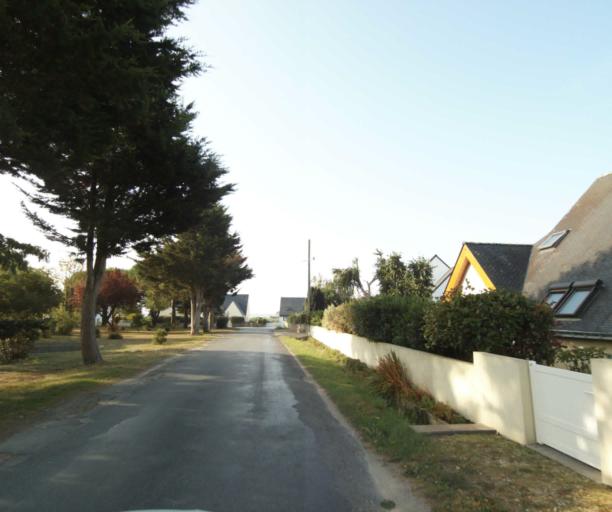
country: FR
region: Brittany
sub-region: Departement du Morbihan
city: Riantec
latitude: 47.7047
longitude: -3.2960
